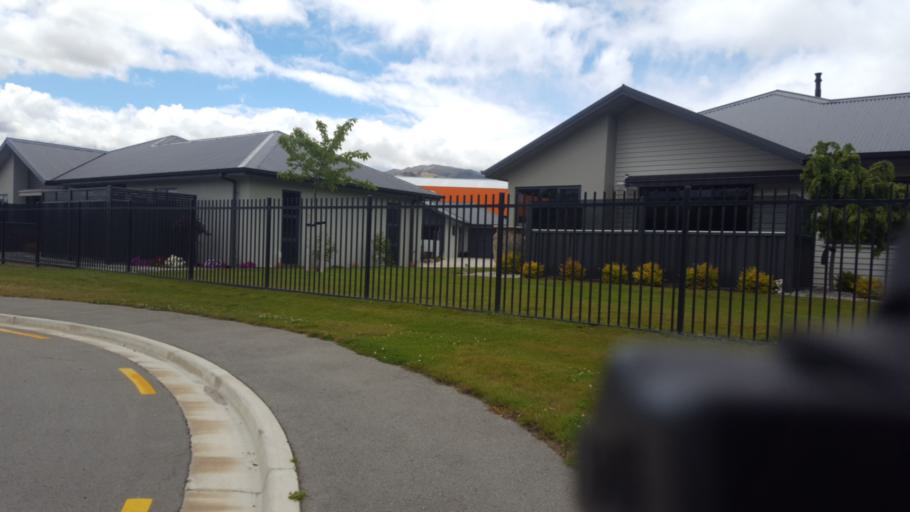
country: NZ
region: Otago
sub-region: Queenstown-Lakes District
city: Wanaka
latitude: -45.0360
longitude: 169.1910
